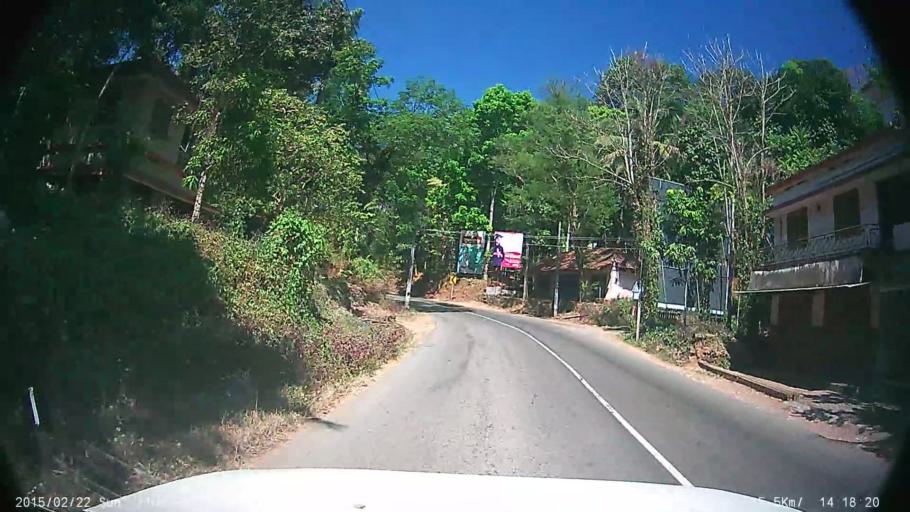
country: IN
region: Kerala
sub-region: Kottayam
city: Lalam
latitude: 9.5641
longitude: 76.6867
